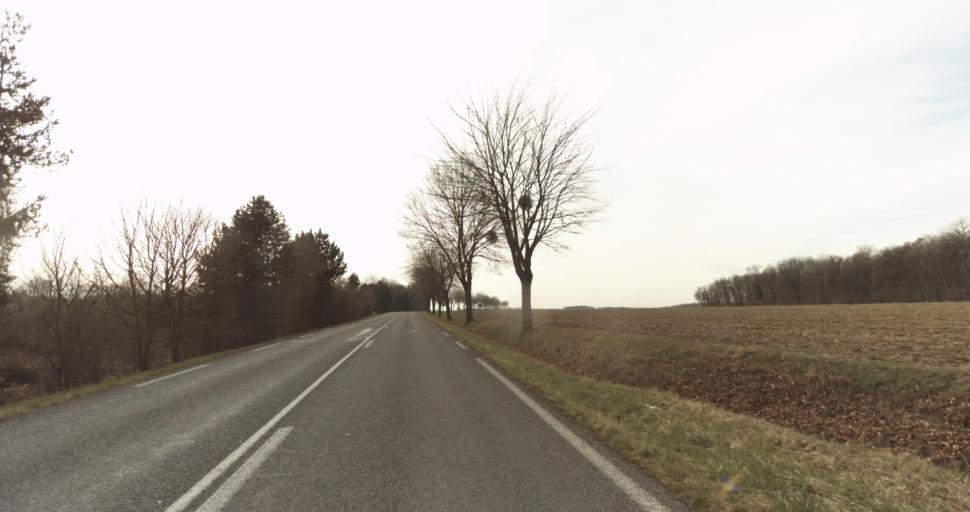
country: FR
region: Lorraine
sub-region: Departement de Meurthe-et-Moselle
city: Jarny
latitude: 49.1346
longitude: 5.8928
